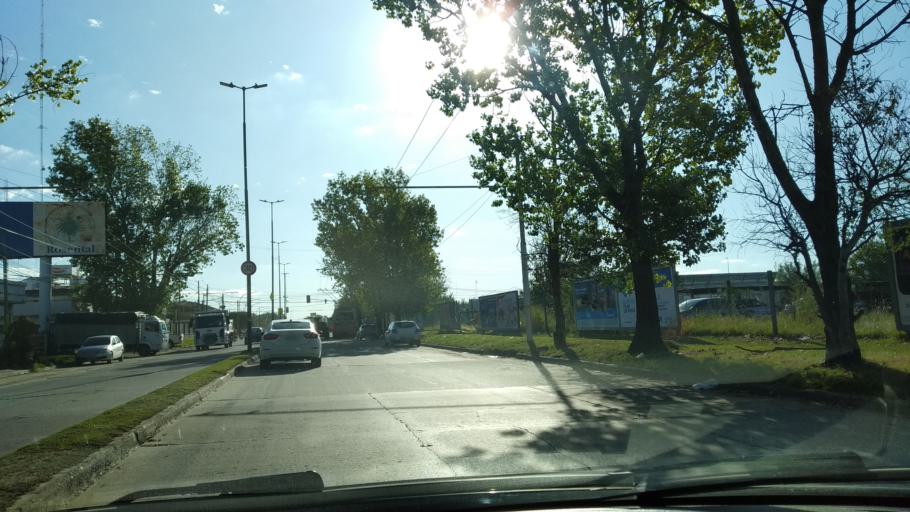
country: AR
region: Santa Fe
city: Perez
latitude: -32.9403
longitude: -60.7369
